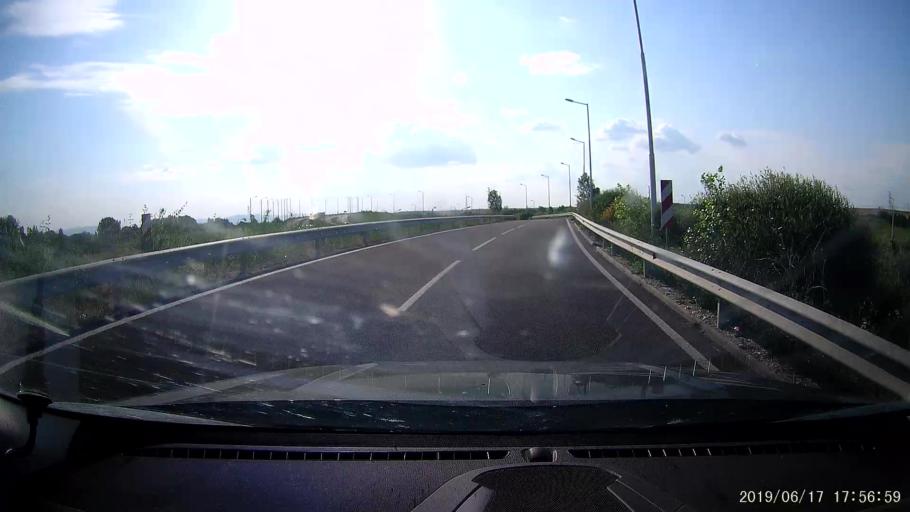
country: GR
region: East Macedonia and Thrace
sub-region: Nomos Evrou
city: Rizia
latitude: 41.7203
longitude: 26.3410
